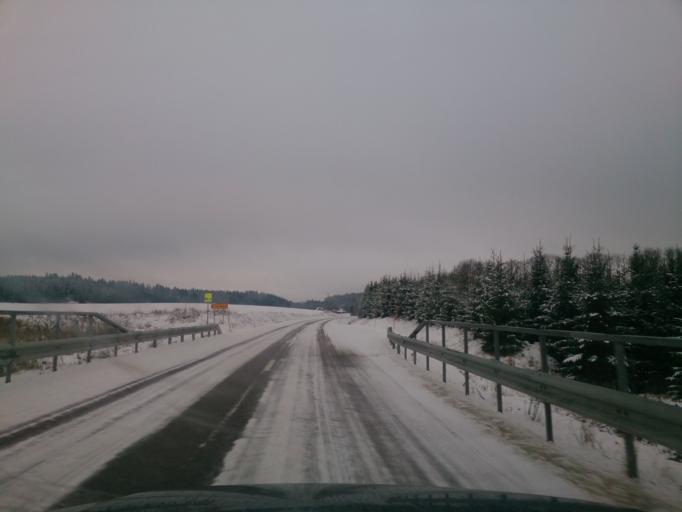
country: SE
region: OEstergoetland
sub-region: Linkopings Kommun
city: Linghem
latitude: 58.4503
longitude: 15.8884
